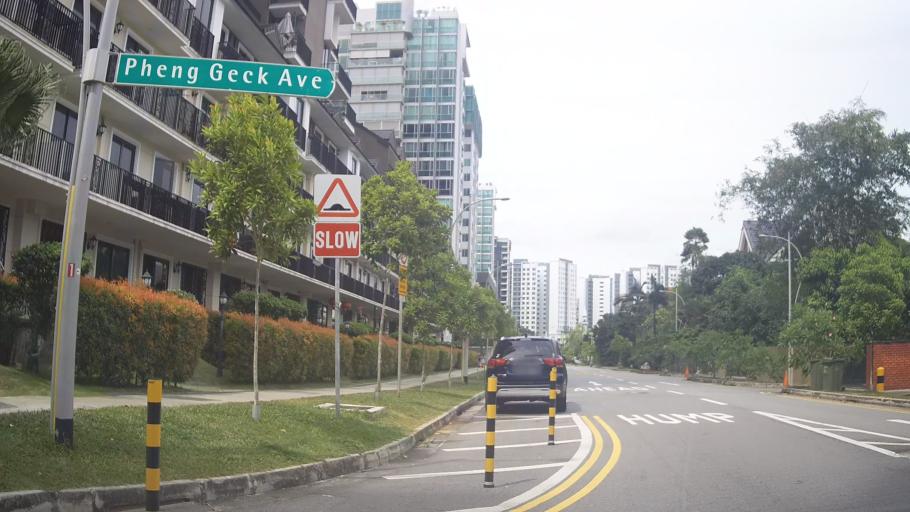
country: SG
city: Singapore
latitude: 1.3292
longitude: 103.8694
